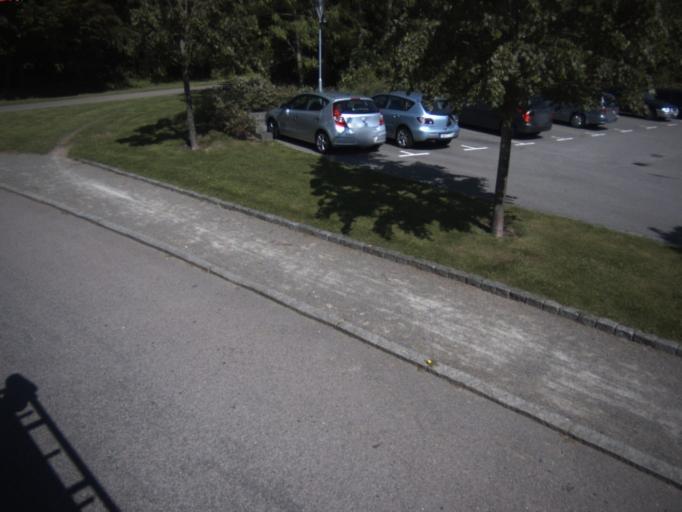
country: SE
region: Skane
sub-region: Helsingborg
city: Helsingborg
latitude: 56.0696
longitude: 12.7123
